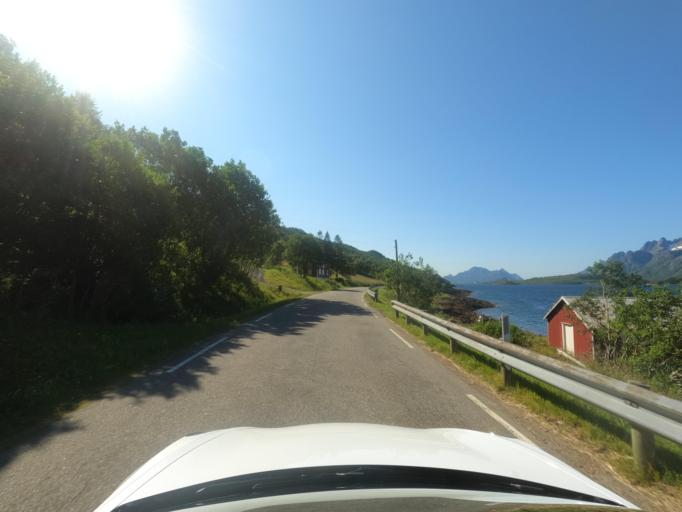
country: NO
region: Nordland
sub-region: Hadsel
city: Stokmarknes
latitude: 68.3823
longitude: 15.0897
